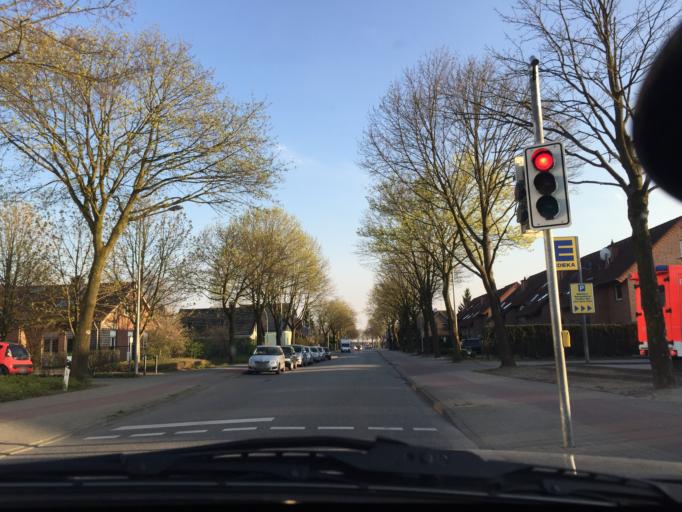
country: DE
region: North Rhine-Westphalia
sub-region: Regierungsbezirk Dusseldorf
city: Kleve
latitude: 51.7701
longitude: 6.1326
